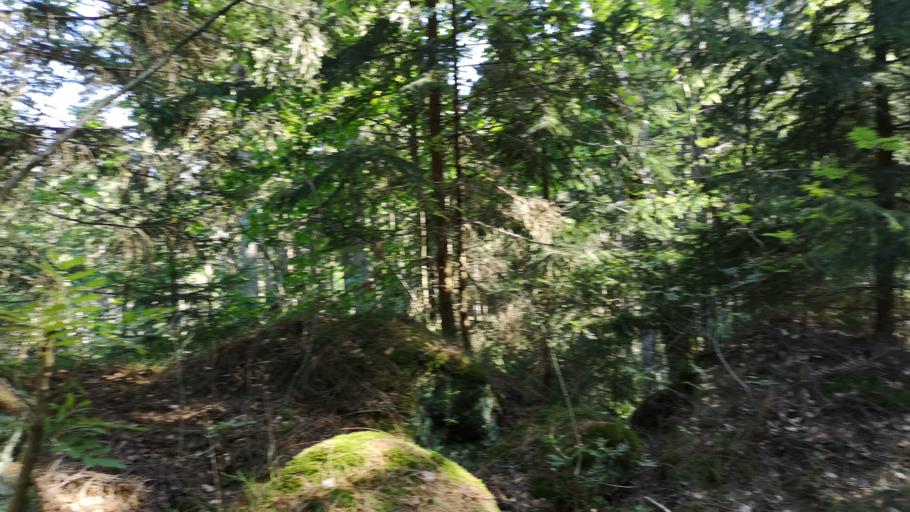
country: DE
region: Saxony
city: Kurort Oybin
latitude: 50.8418
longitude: 14.7602
